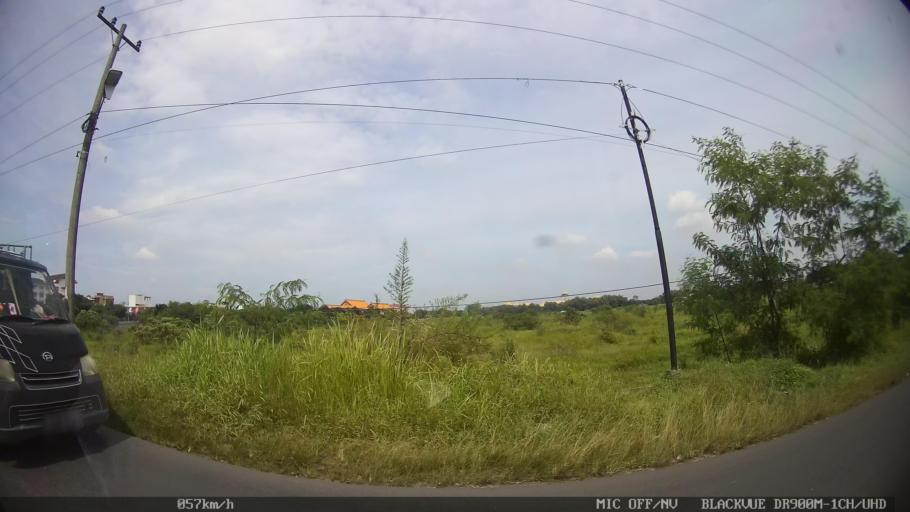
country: ID
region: North Sumatra
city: Medan
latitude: 3.6380
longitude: 98.7075
